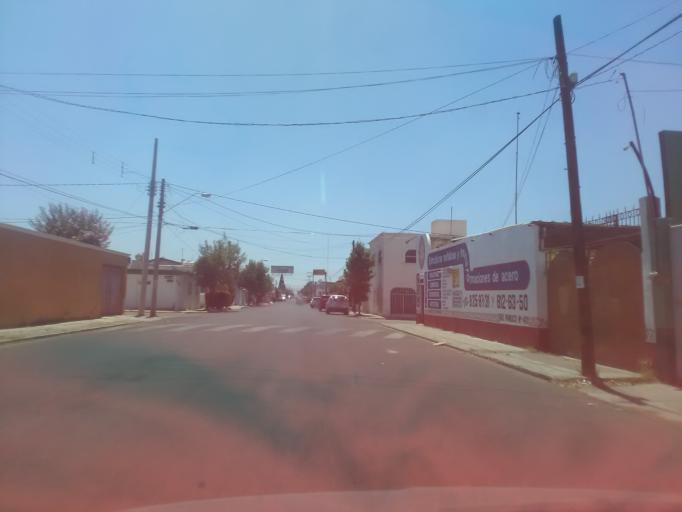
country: MX
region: Durango
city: Victoria de Durango
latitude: 24.0128
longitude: -104.6817
